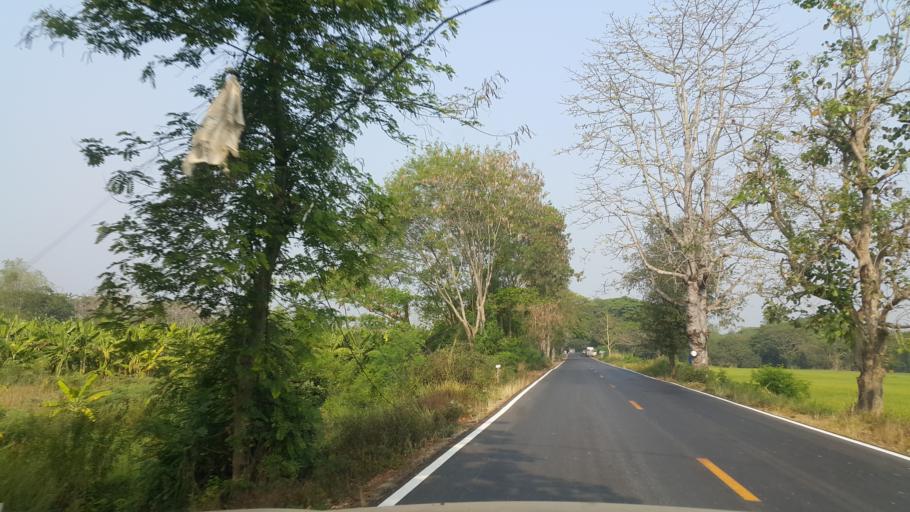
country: TH
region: Chiang Mai
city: Saraphi
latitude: 18.6762
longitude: 99.0783
